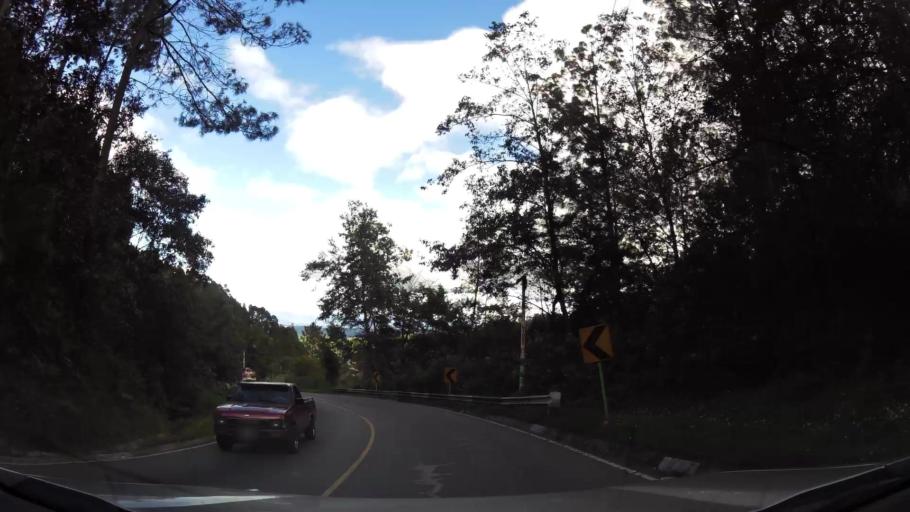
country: GT
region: Quiche
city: Chichicastenango
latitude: 14.9122
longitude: -91.1007
